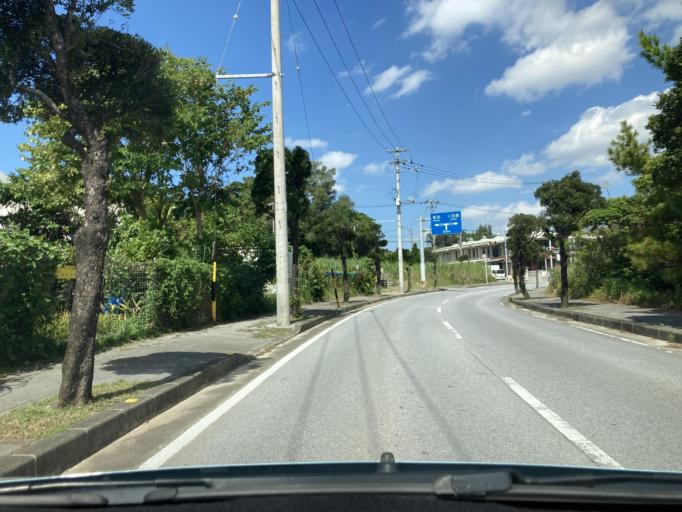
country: JP
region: Okinawa
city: Ginowan
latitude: 26.2283
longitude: 127.7507
